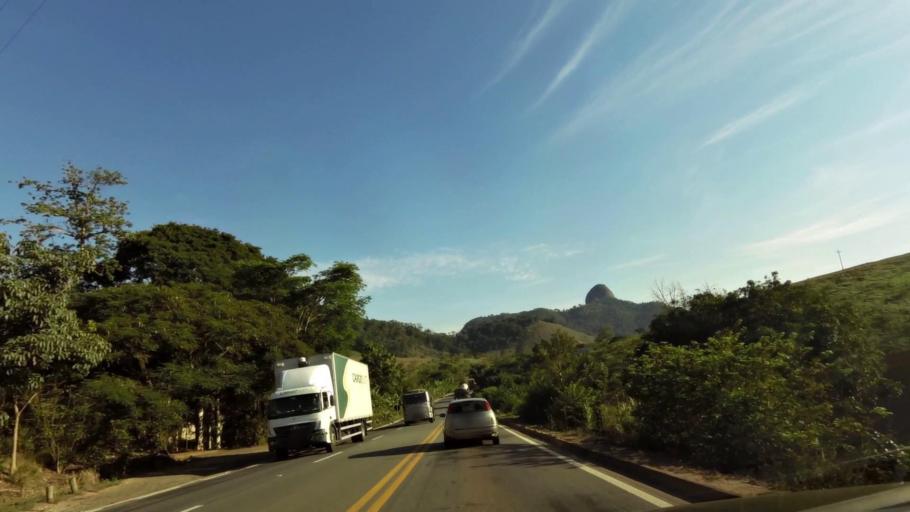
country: BR
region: Espirito Santo
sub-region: Guarapari
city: Guarapari
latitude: -20.5361
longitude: -40.4830
